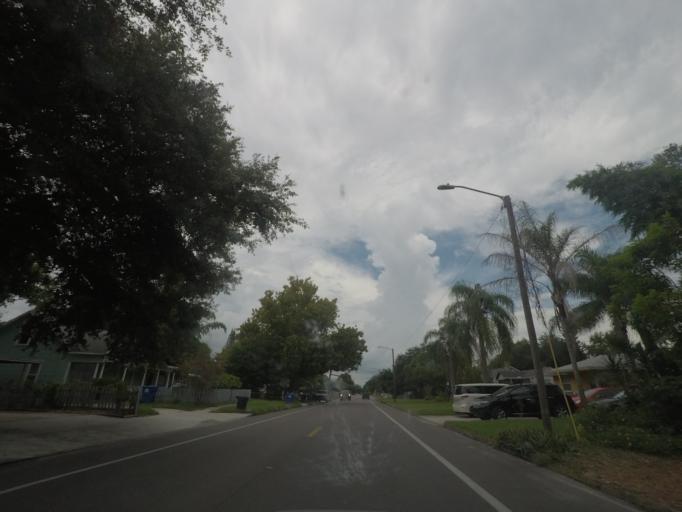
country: US
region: Florida
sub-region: Pinellas County
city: Lealman
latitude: 27.7993
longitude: -82.6577
